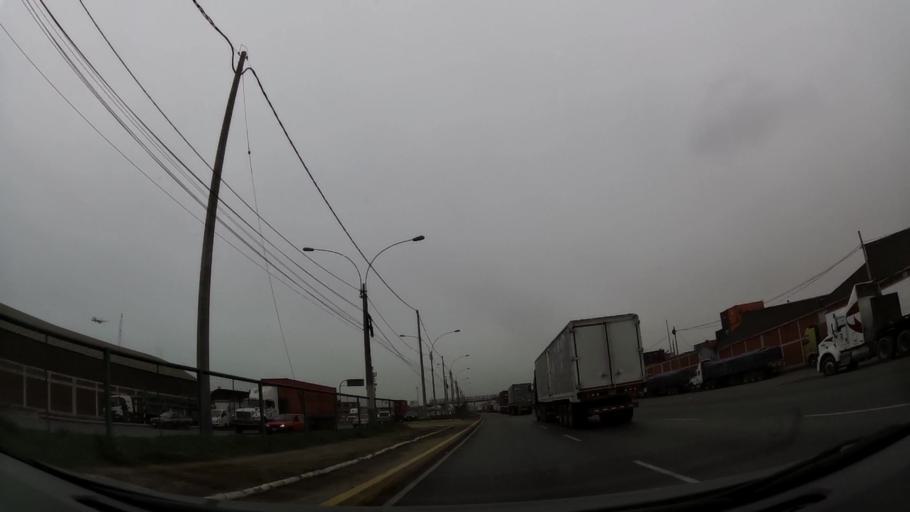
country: PE
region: Callao
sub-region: Callao
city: Callao
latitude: -11.9924
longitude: -77.1256
